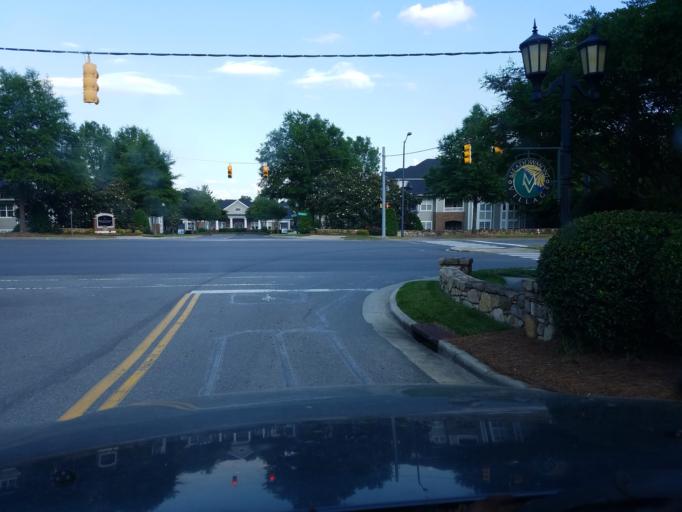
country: US
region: North Carolina
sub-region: Orange County
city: Chapel Hill
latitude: 35.9047
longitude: -79.0098
